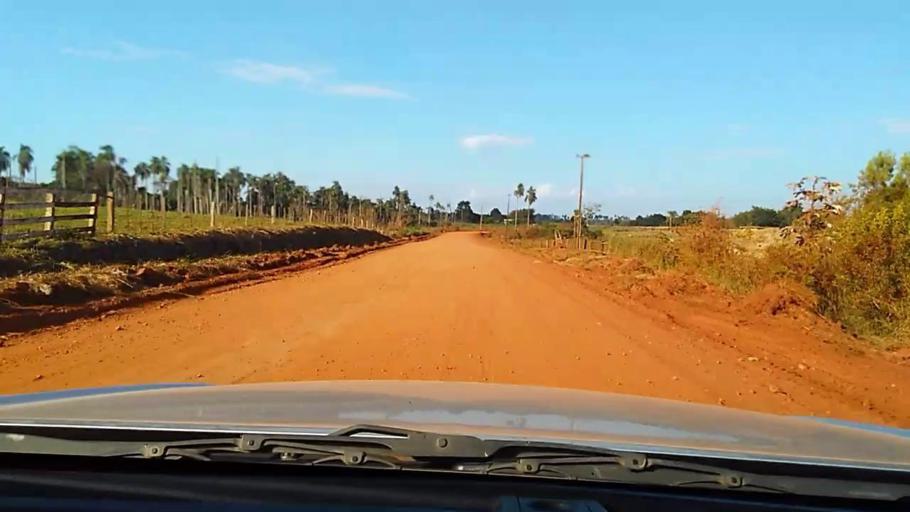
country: PY
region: Alto Parana
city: Doctor Juan Leon Mallorquin
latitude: -25.7038
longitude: -55.3821
